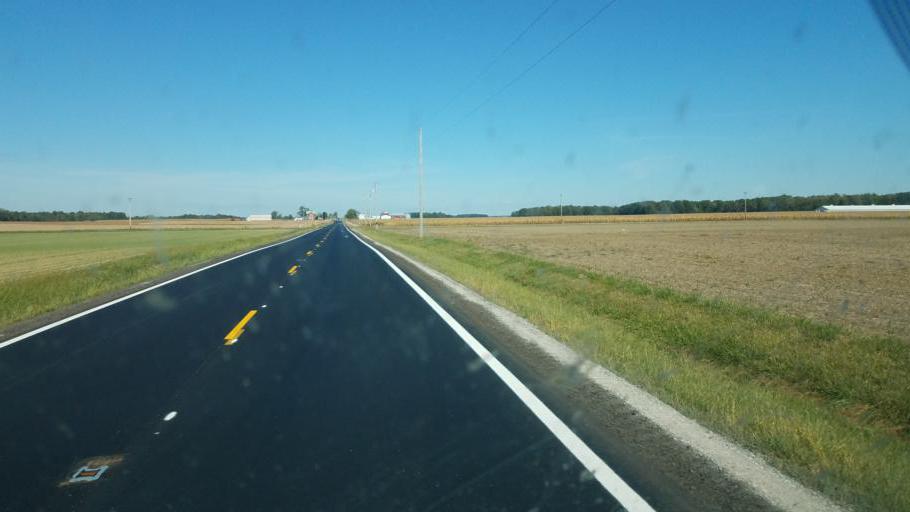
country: US
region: Ohio
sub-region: Crawford County
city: Bucyrus
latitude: 40.9337
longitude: -83.0165
